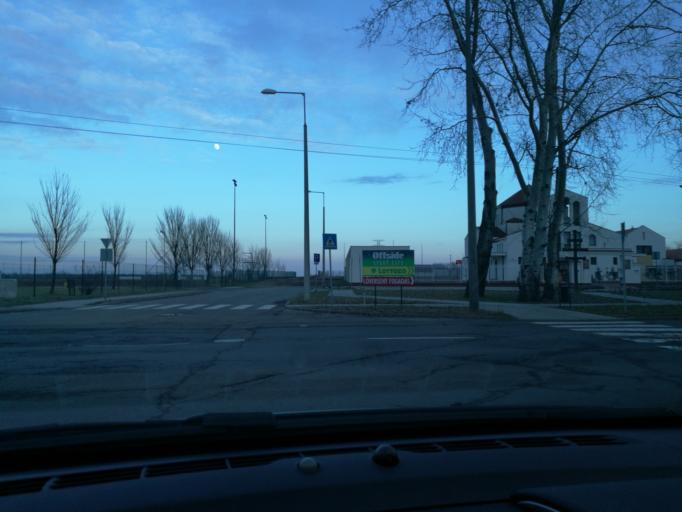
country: HU
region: Szabolcs-Szatmar-Bereg
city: Nyiregyhaza
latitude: 47.9620
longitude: 21.7438
